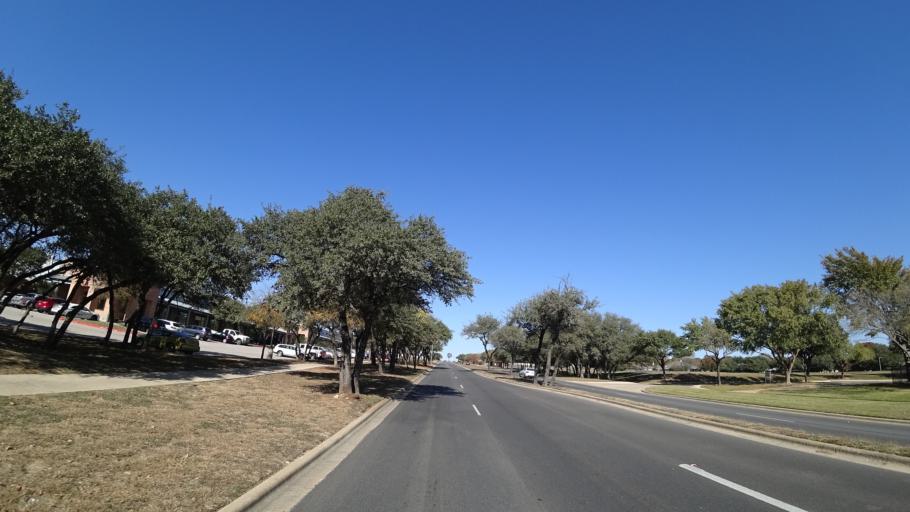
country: US
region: Texas
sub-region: Williamson County
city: Cedar Park
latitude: 30.5163
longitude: -97.8519
